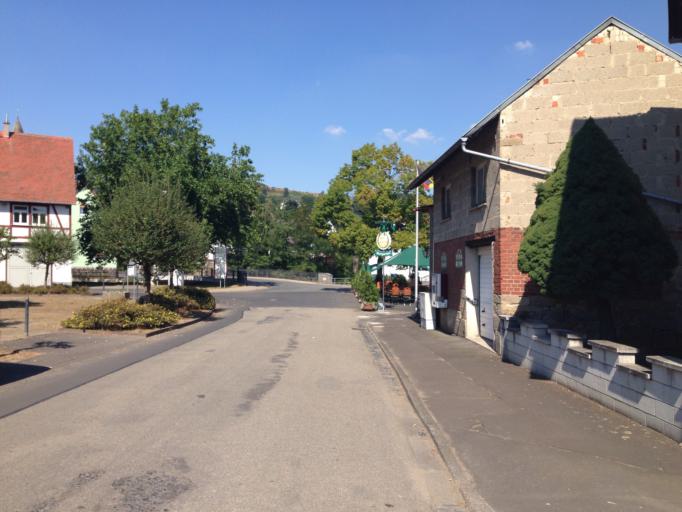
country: DE
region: Hesse
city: Beuern
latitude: 50.6657
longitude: 8.7855
